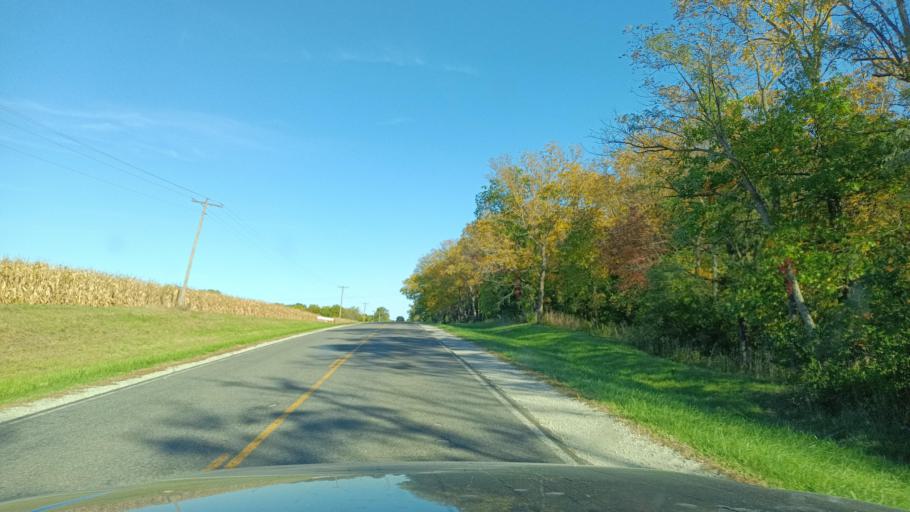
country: US
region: Illinois
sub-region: McLean County
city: Le Roy
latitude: 40.2245
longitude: -88.8319
